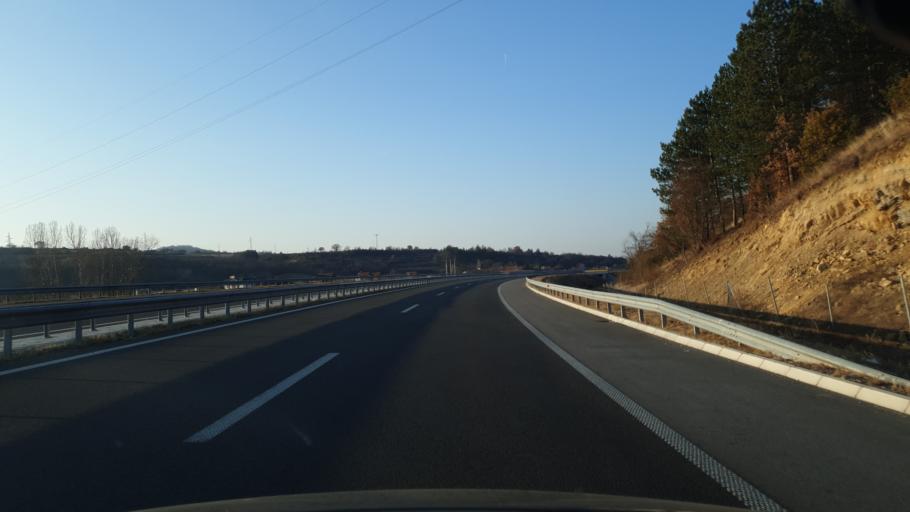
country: RS
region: Central Serbia
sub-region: Pirotski Okrug
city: Dimitrovgrad
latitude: 43.0247
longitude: 22.7262
